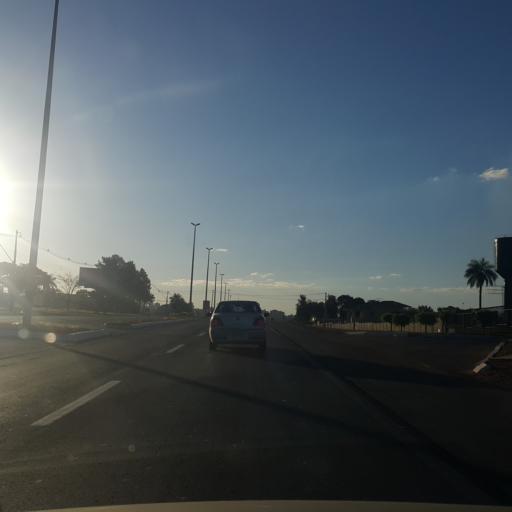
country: BR
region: Federal District
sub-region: Brasilia
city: Brasilia
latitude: -15.8581
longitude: -47.9889
